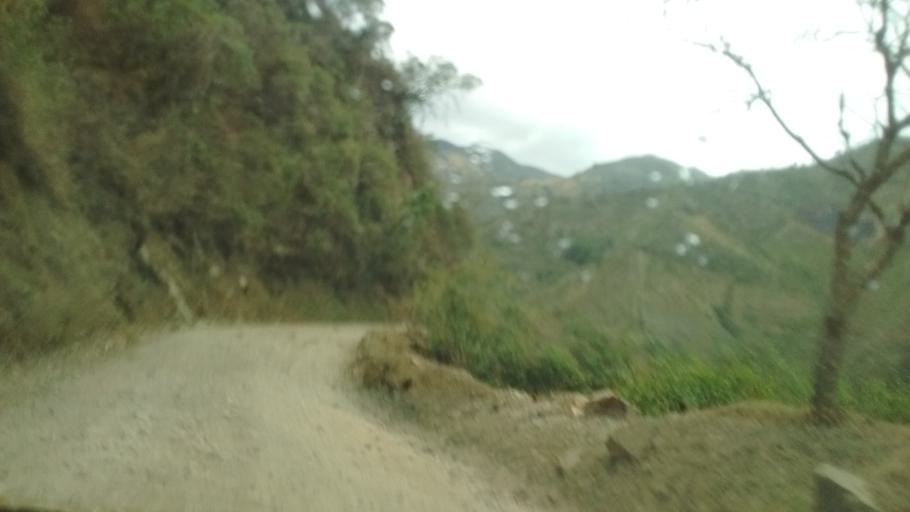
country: CO
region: Cauca
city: La Vega
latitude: 2.0314
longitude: -76.7987
